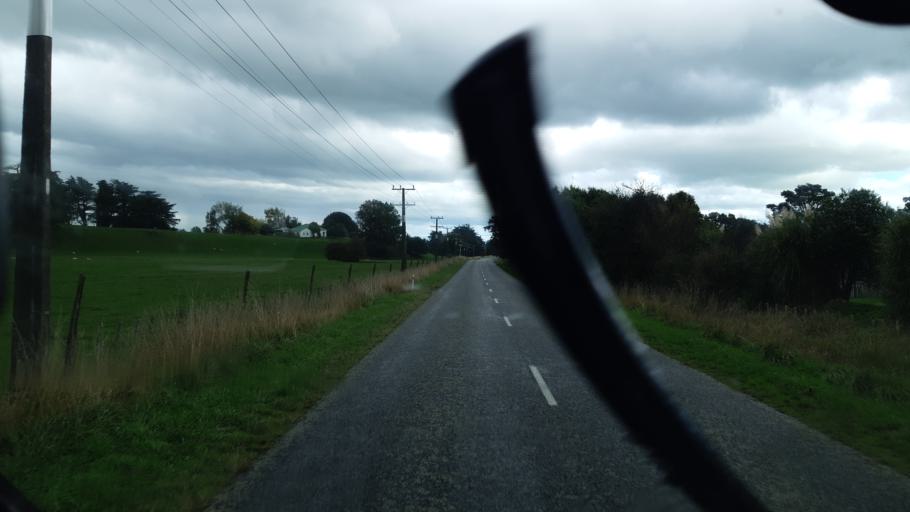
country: NZ
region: Manawatu-Wanganui
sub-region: Palmerston North City
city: Palmerston North
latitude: -40.1515
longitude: 175.6039
